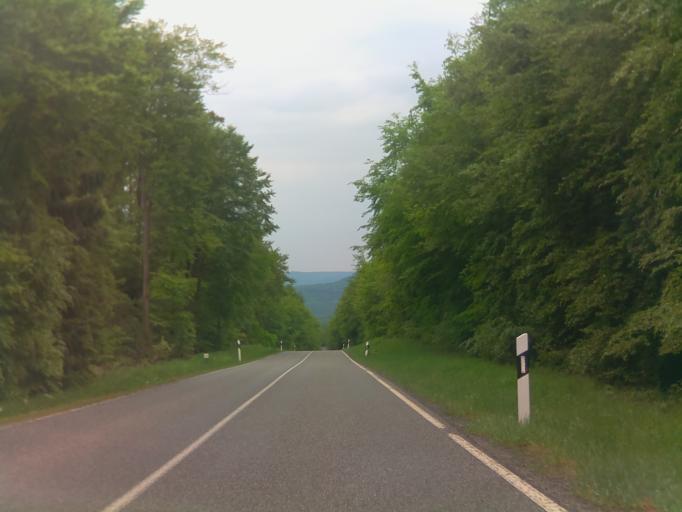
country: DE
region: Hesse
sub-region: Regierungsbezirk Darmstadt
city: Glashutten
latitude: 50.2055
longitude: 8.4018
